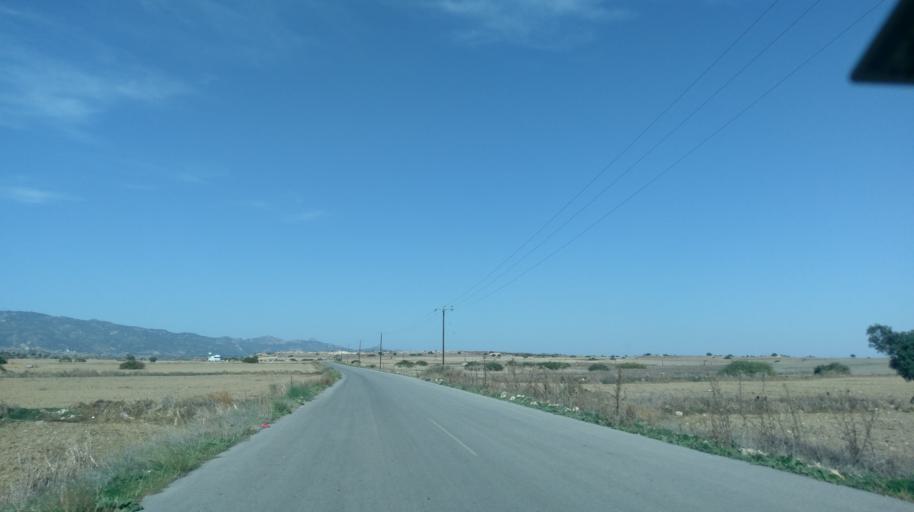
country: CY
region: Ammochostos
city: Trikomo
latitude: 35.3062
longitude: 33.8913
